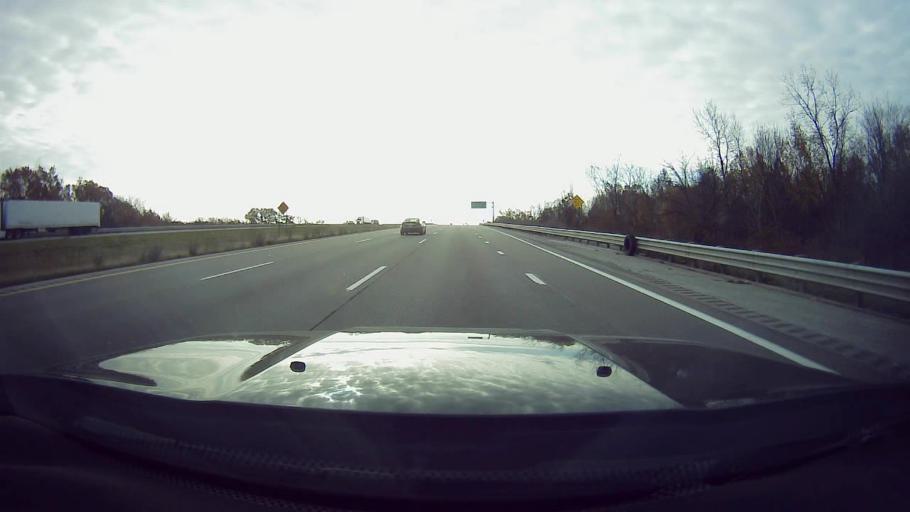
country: US
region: Michigan
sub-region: Monroe County
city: Carleton
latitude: 42.0718
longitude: -83.3669
